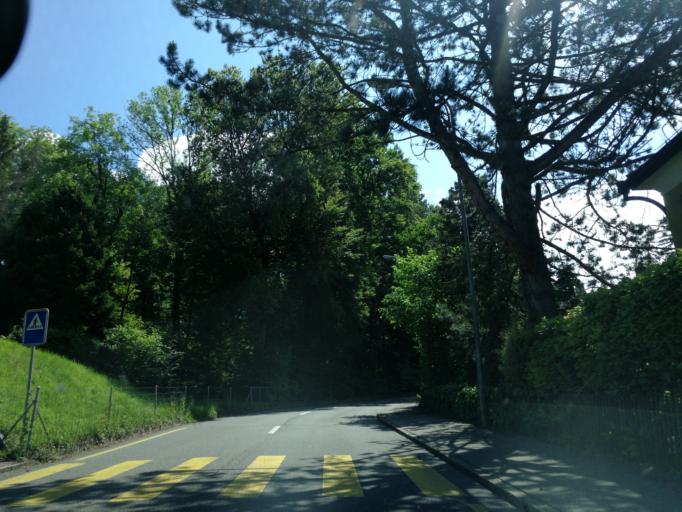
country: CH
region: Zurich
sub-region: Bezirk Meilen
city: Kuesnacht
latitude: 47.3230
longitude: 8.5838
